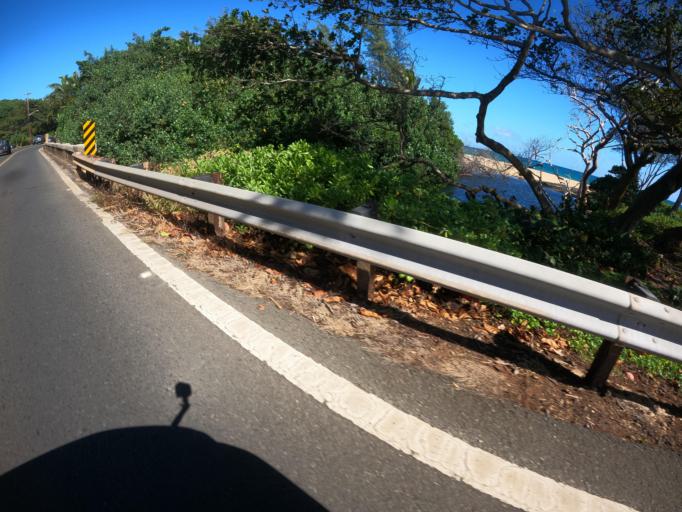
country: US
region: Hawaii
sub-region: Honolulu County
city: La'ie
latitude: 21.6326
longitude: -157.9213
